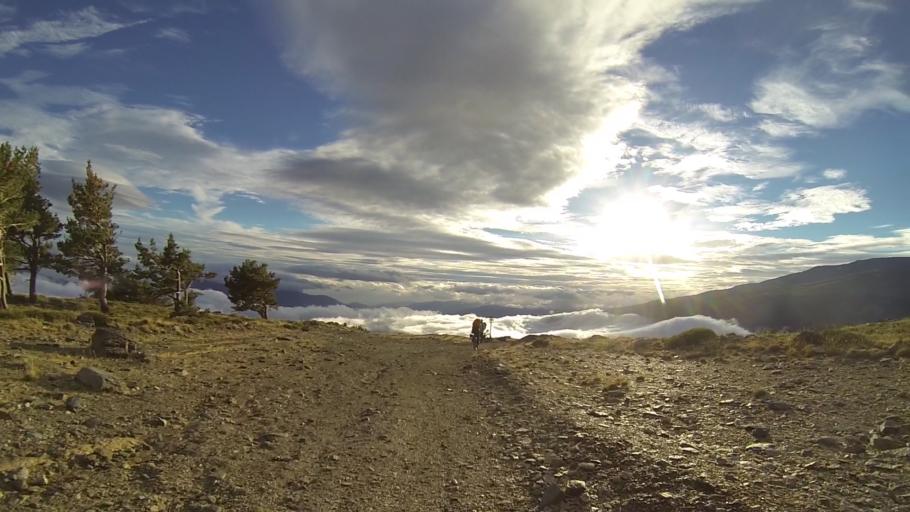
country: ES
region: Andalusia
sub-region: Provincia de Granada
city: Capileira
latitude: 36.9780
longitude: -3.3303
